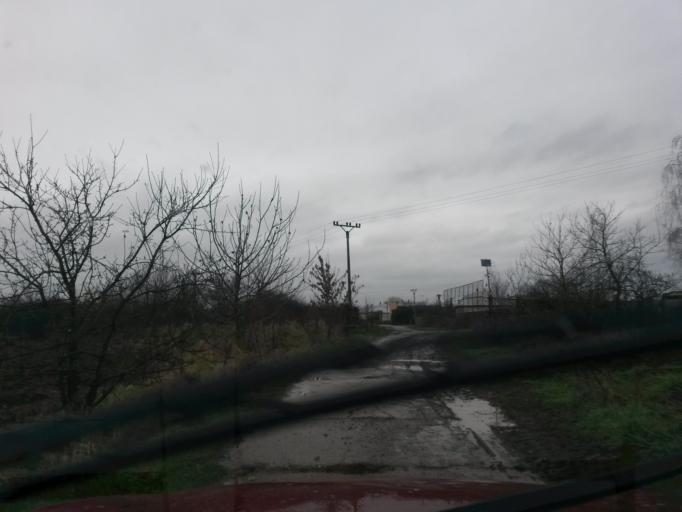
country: UA
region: Zakarpattia
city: Storozhnytsya
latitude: 48.6283
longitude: 22.1027
